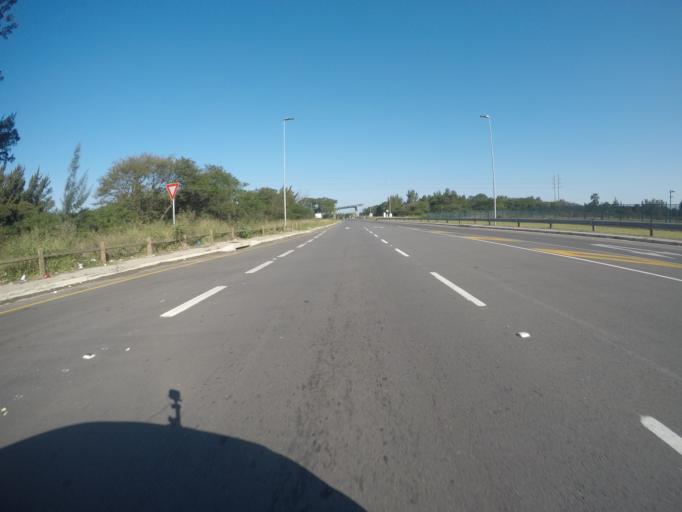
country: ZA
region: KwaZulu-Natal
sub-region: uThungulu District Municipality
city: Richards Bay
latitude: -28.7802
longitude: 32.0674
